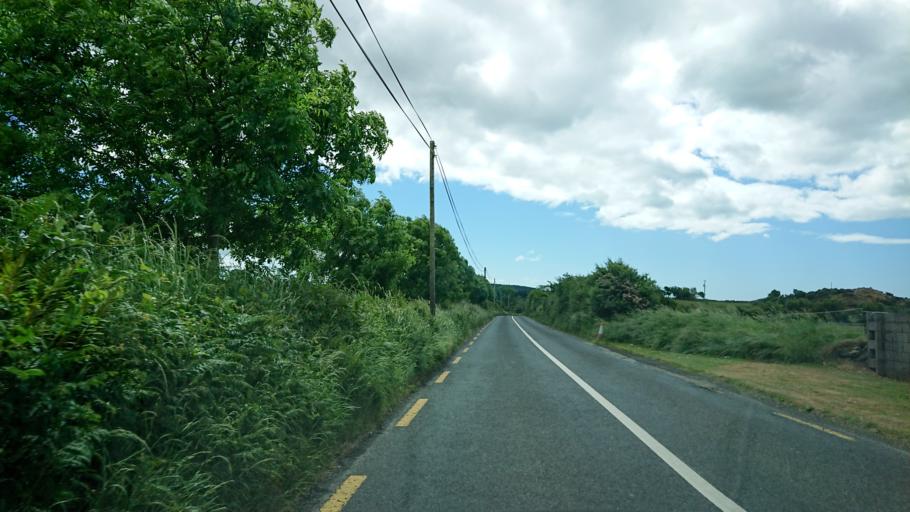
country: IE
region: Munster
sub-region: Waterford
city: Tra Mhor
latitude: 52.1918
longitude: -7.1836
